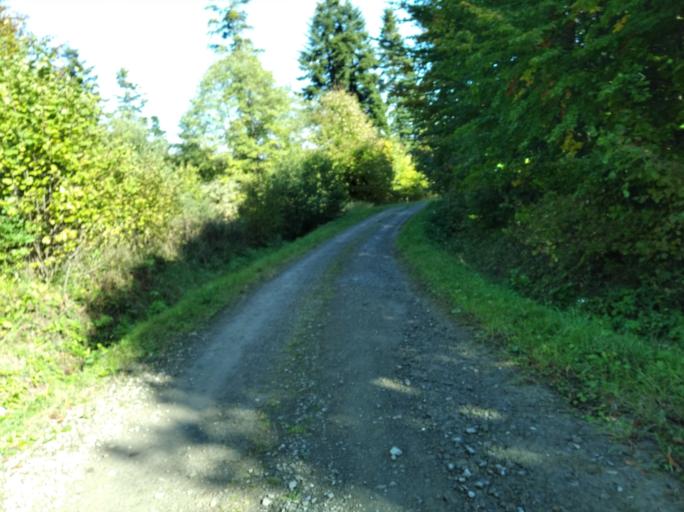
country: PL
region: Subcarpathian Voivodeship
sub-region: Powiat strzyzowski
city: Strzyzow
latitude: 49.8276
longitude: 21.7923
